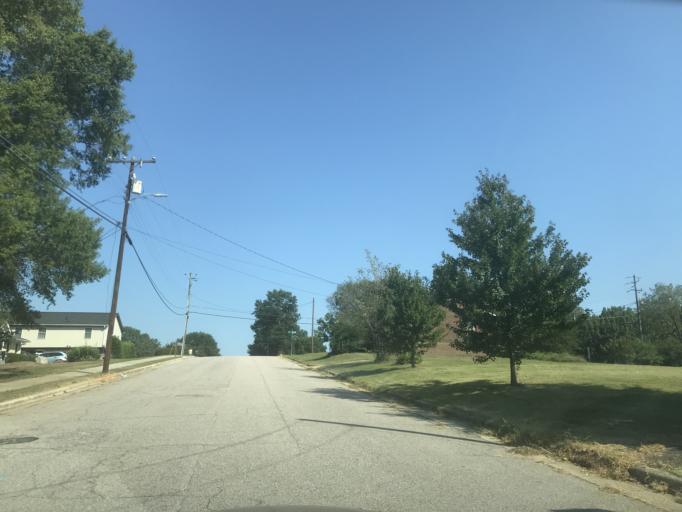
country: US
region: North Carolina
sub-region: Wake County
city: Raleigh
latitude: 35.7639
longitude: -78.6293
